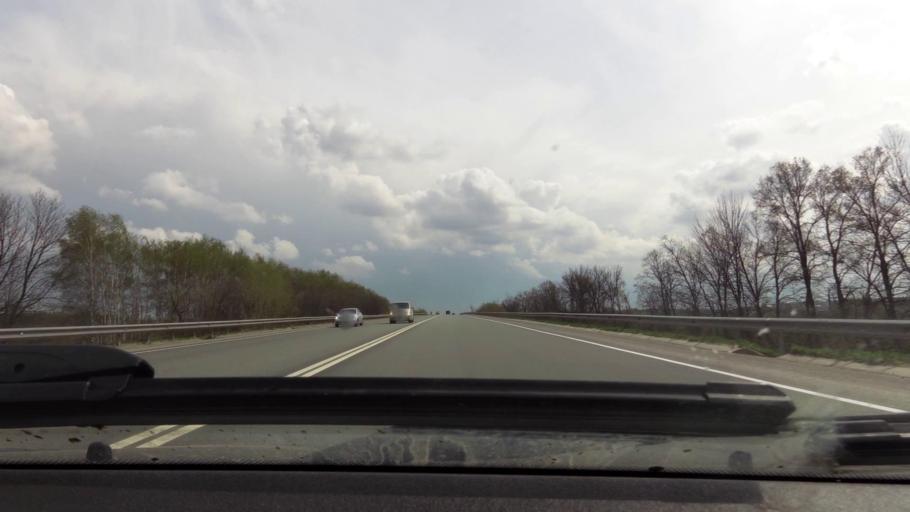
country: RU
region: Rjazan
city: Bagramovo
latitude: 54.7387
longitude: 39.4475
